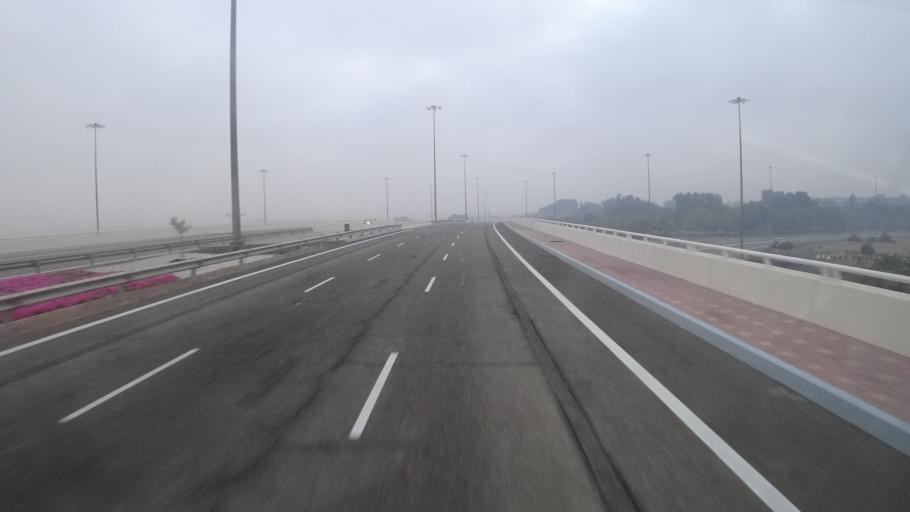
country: AE
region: Abu Dhabi
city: Abu Dhabi
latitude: 24.2416
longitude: 54.7006
